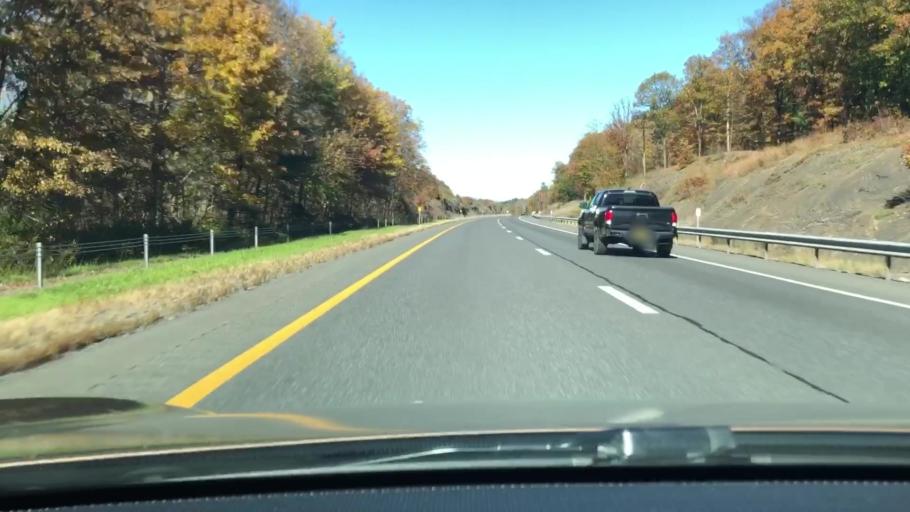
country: US
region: New York
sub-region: Ulster County
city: Tillson
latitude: 41.7961
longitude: -74.0516
